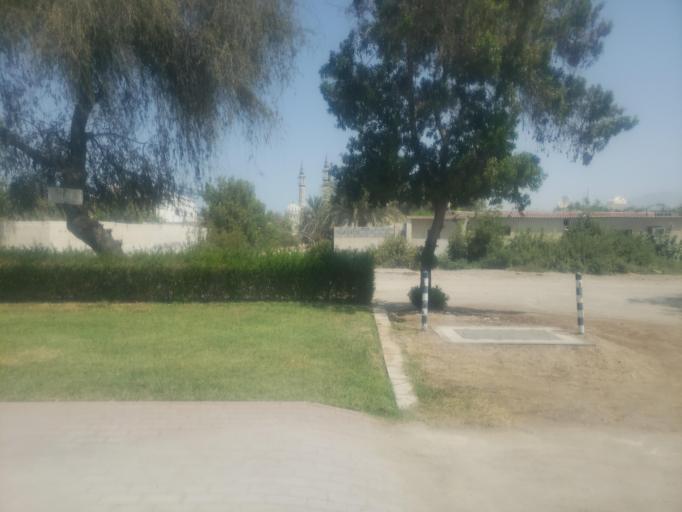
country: AE
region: Ra's al Khaymah
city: Ras al-Khaimah
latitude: 25.8028
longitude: 55.9708
